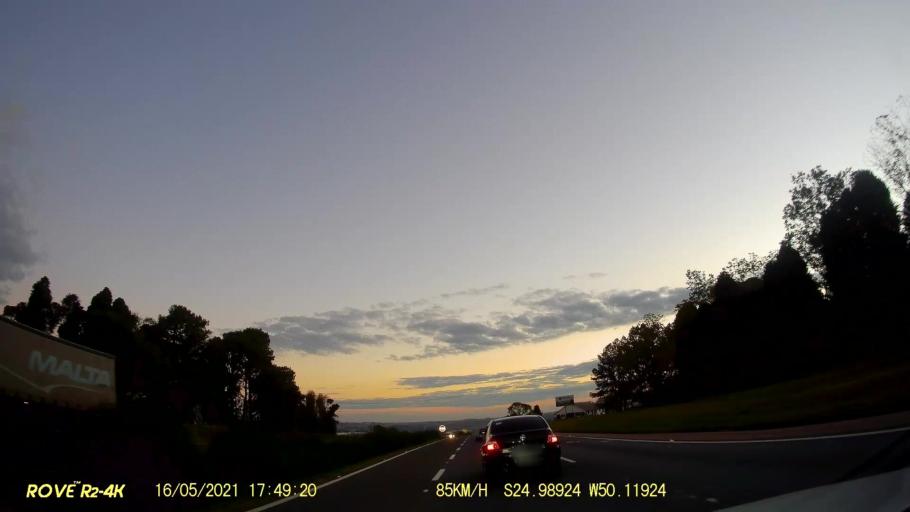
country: BR
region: Parana
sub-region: Carambei
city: Carambei
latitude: -24.9892
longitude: -50.1194
